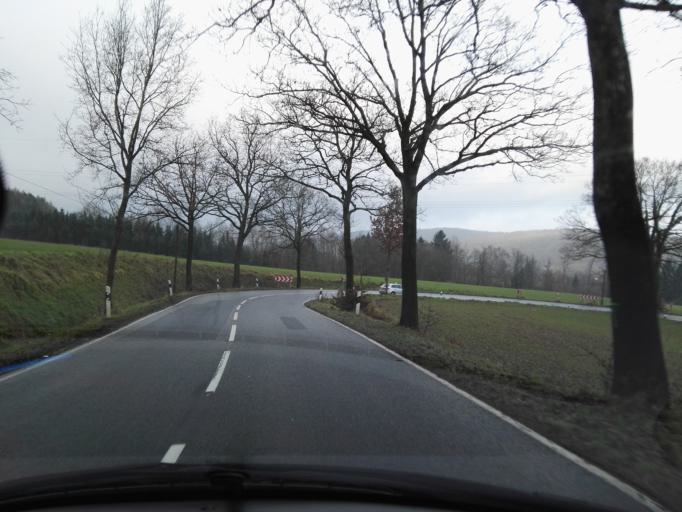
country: DE
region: Lower Saxony
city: Diekholzen
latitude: 52.0835
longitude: 9.9077
